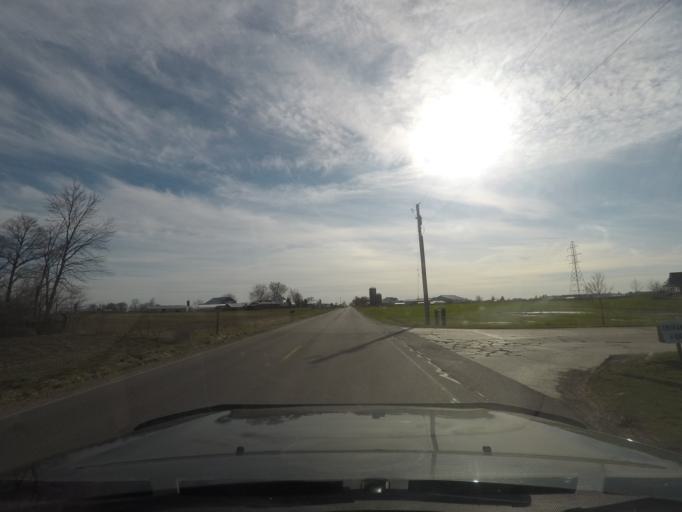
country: US
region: Indiana
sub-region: Elkhart County
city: Wakarusa
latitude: 41.5261
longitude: -85.9592
